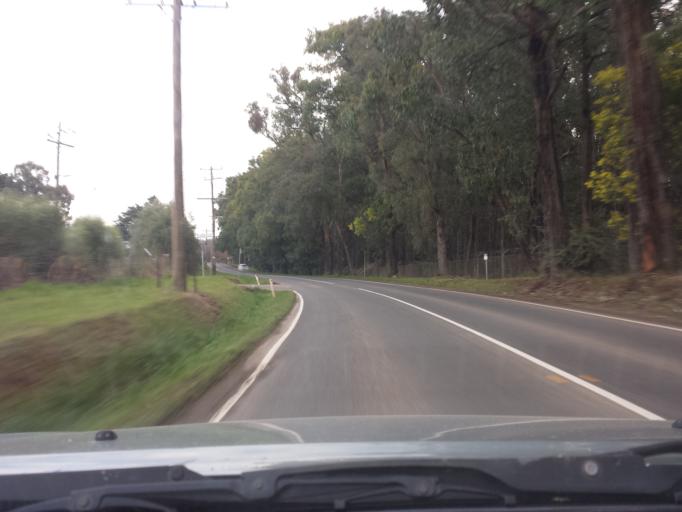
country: AU
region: Victoria
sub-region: Yarra Ranges
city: Monbulk
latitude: -37.8420
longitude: 145.4248
